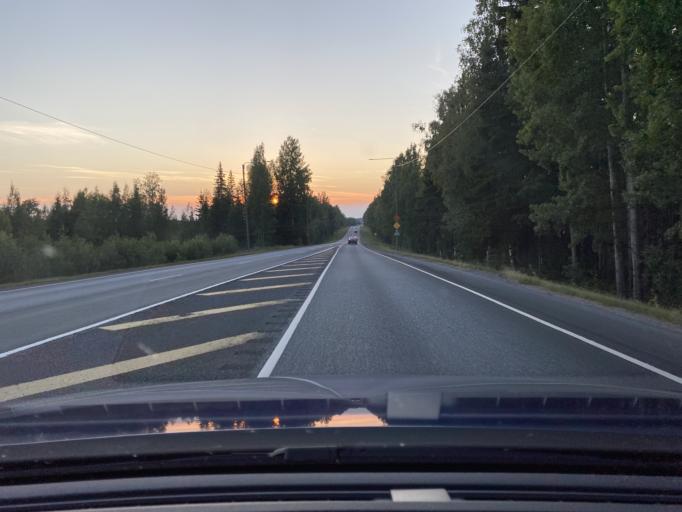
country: FI
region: Pirkanmaa
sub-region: Luoteis-Pirkanmaa
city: Ikaalinen
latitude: 61.7887
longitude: 22.9911
